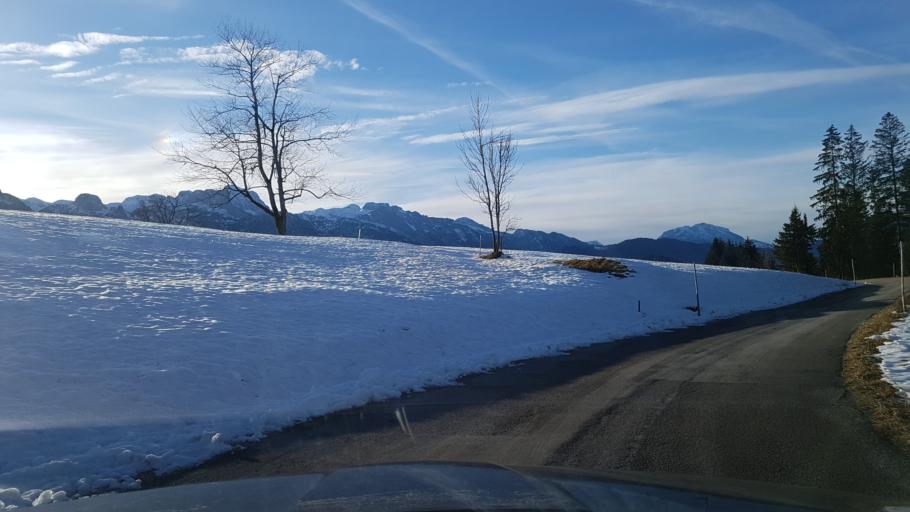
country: AT
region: Salzburg
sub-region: Politischer Bezirk Hallein
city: Abtenau
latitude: 47.5702
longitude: 13.4078
